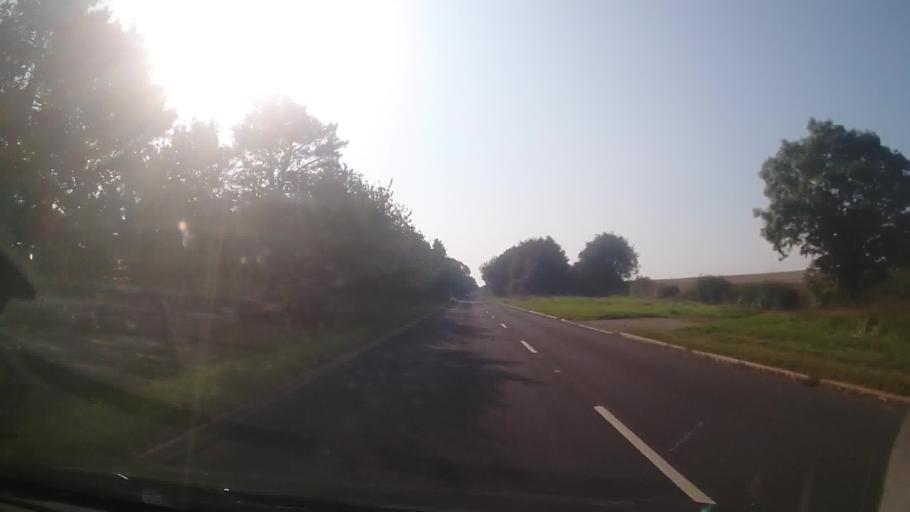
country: GB
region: England
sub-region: Shropshire
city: Much Wenlock
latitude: 52.5829
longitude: -2.5485
